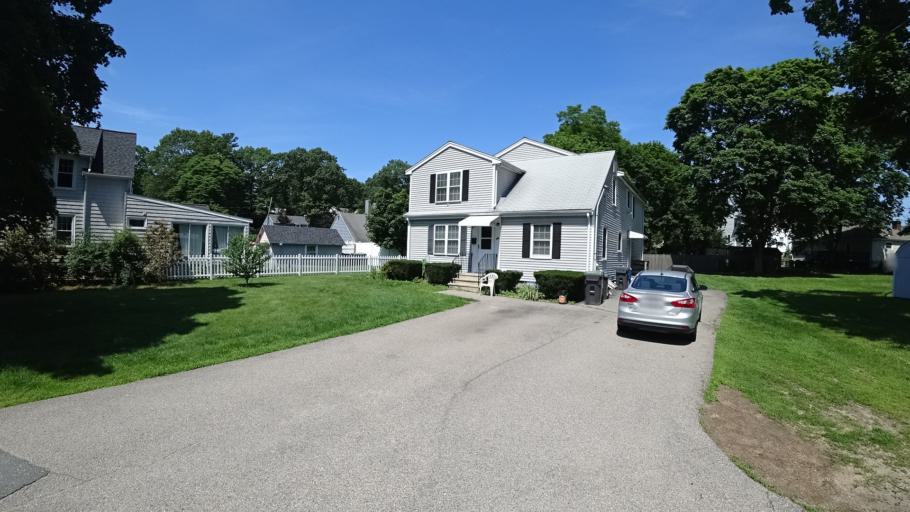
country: US
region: Massachusetts
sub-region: Norfolk County
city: Dedham
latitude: 42.2446
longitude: -71.1572
